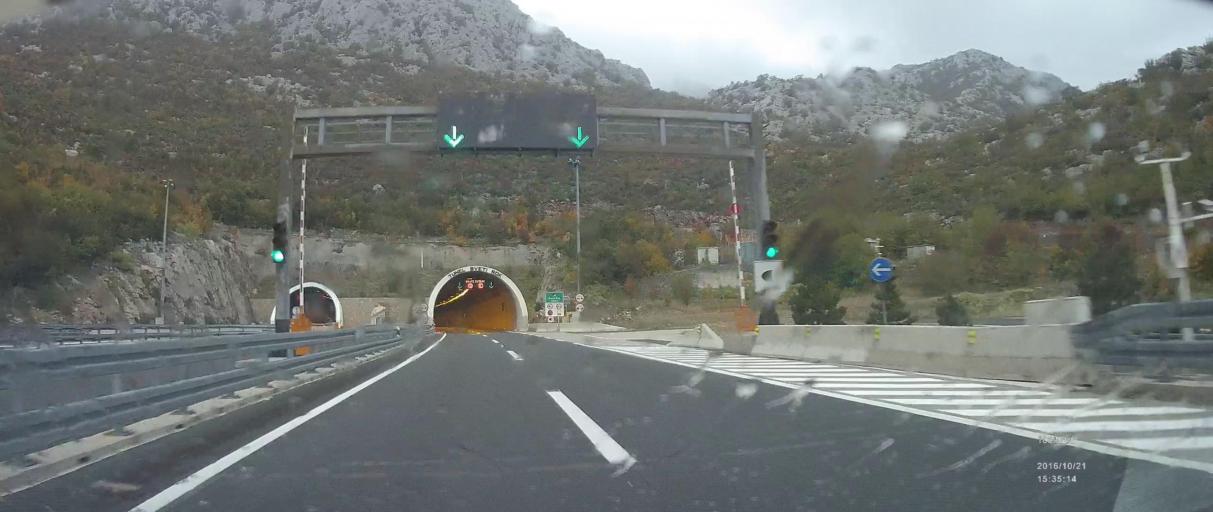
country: HR
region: Zadarska
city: Obrovac
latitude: 44.2549
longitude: 15.6486
